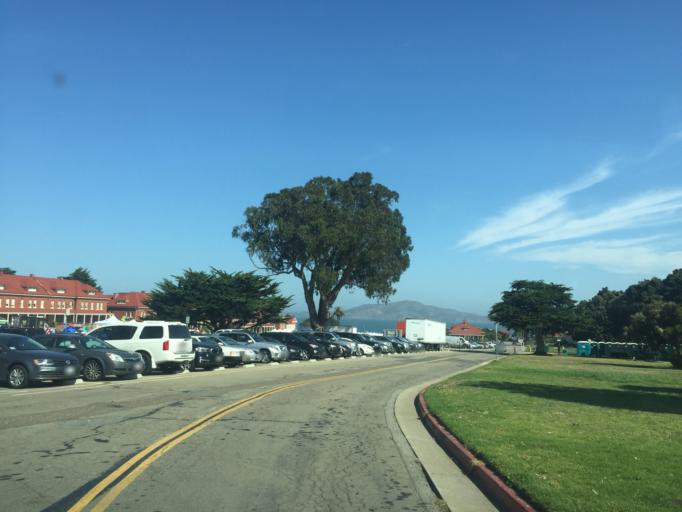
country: US
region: California
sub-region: San Francisco County
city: San Francisco
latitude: 37.7992
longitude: -122.4585
